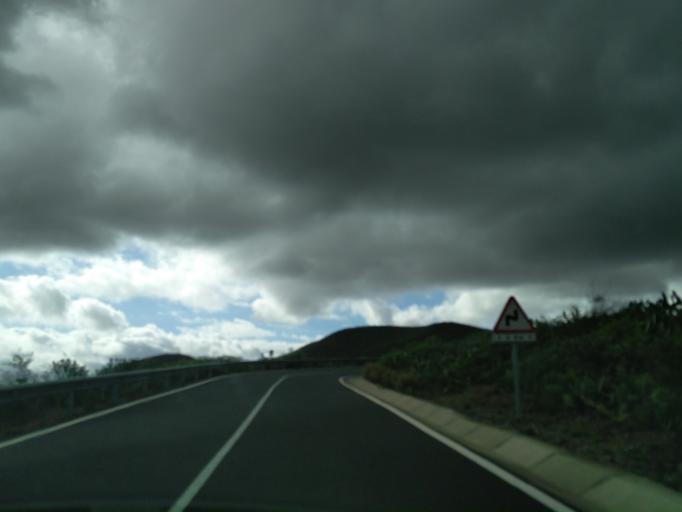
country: ES
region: Canary Islands
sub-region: Provincia de Santa Cruz de Tenerife
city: Arona
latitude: 28.1119
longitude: -16.6844
